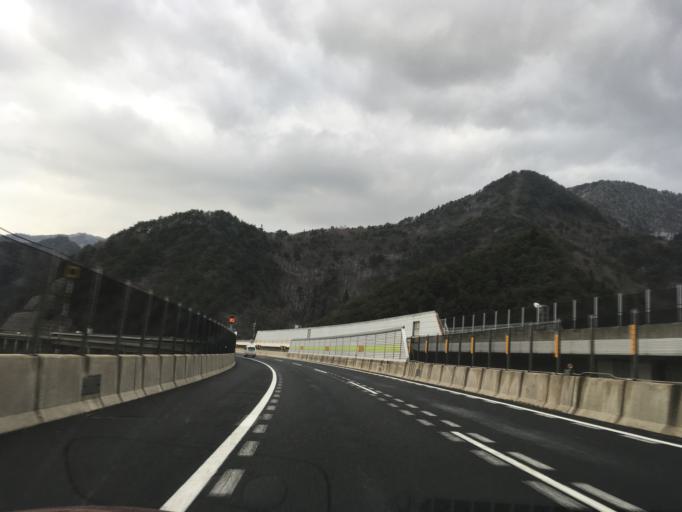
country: JP
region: Yamagata
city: Yamagata-shi
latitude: 38.2347
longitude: 140.4099
